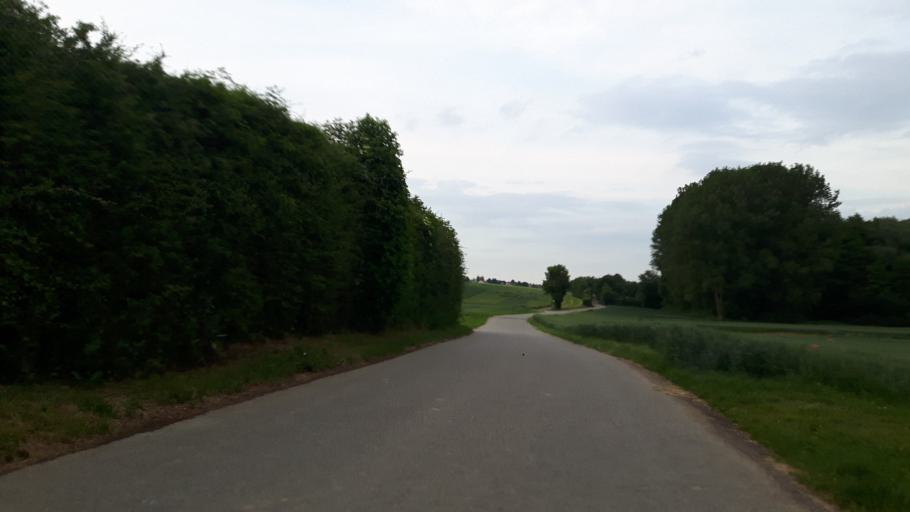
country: DE
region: Bavaria
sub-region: Regierungsbezirk Unterfranken
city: Estenfeld
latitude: 49.8153
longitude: 9.9911
